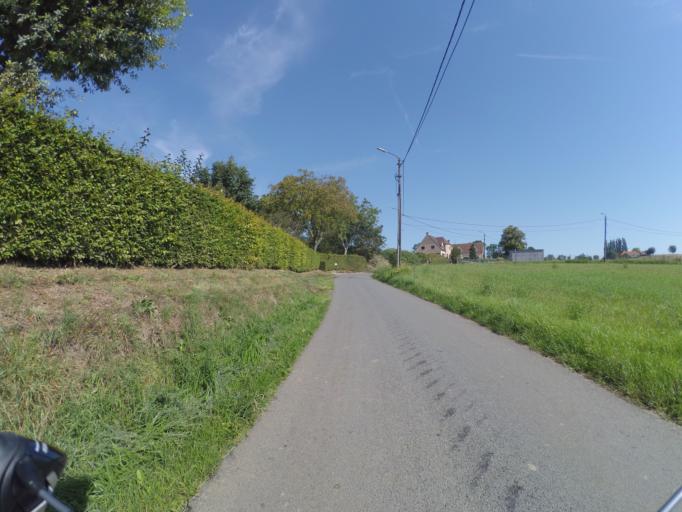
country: BE
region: Flanders
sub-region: Provincie Oost-Vlaanderen
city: Ronse
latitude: 50.7639
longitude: 3.6135
